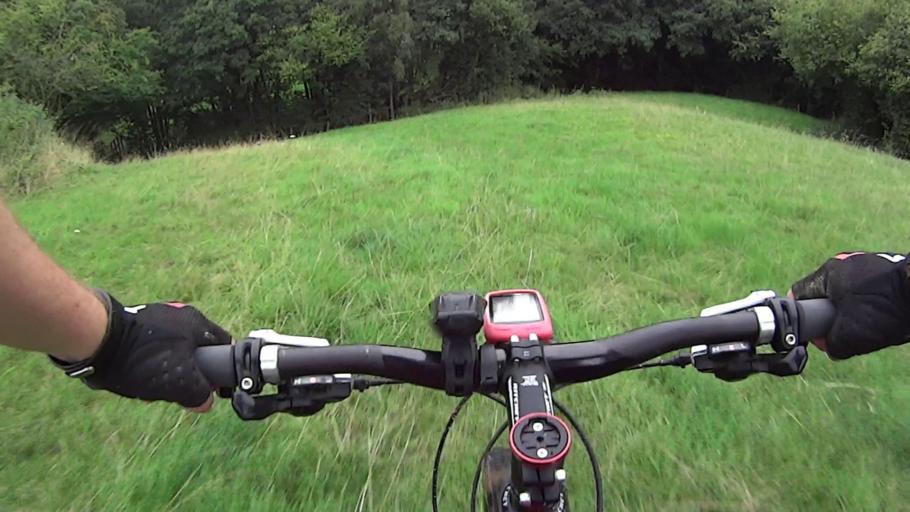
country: GB
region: England
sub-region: Worcestershire
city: Tenbury Wells
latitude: 52.2949
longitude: -2.5855
